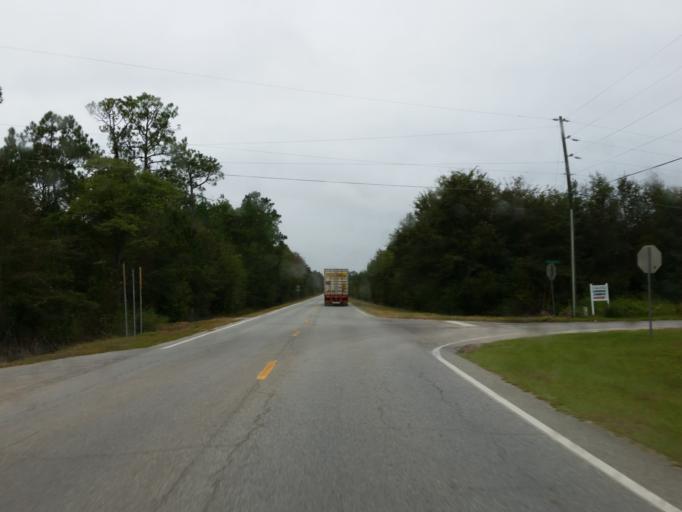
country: US
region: Georgia
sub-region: Berrien County
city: Ray City
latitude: 31.0809
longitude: -83.2272
